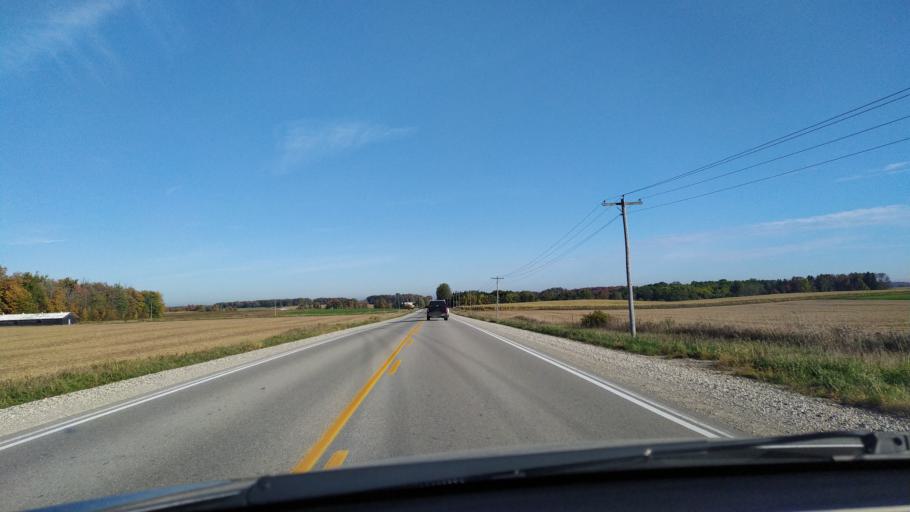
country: CA
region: Ontario
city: Stratford
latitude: 43.4501
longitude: -80.8389
